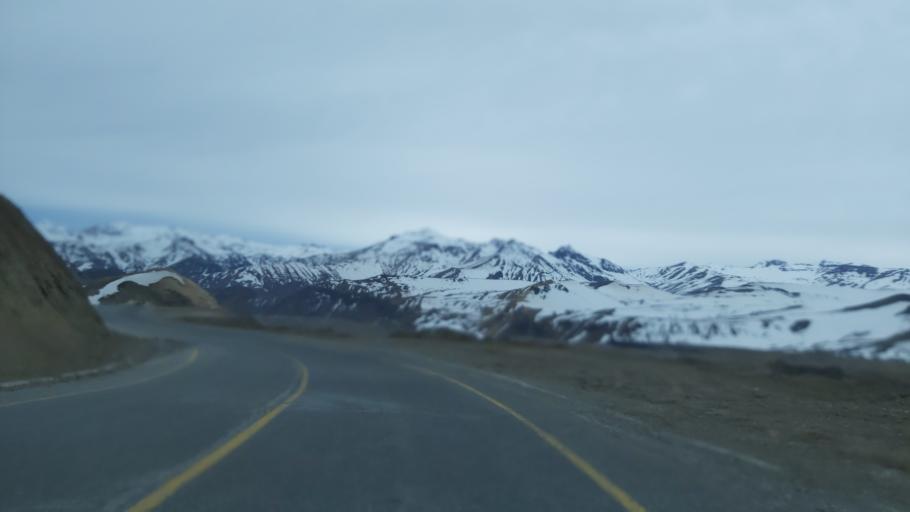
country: CL
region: Maule
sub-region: Provincia de Linares
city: Colbun
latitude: -35.9875
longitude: -70.5600
